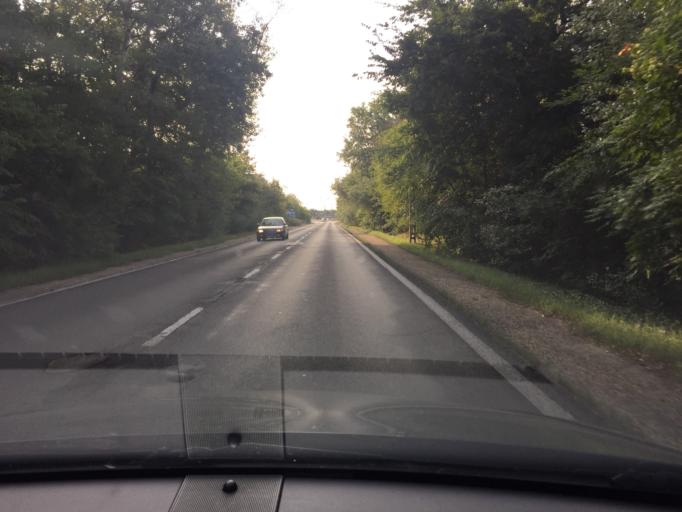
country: HU
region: Budapest
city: Budapest XVI. keruelet
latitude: 47.5389
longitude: 19.1569
